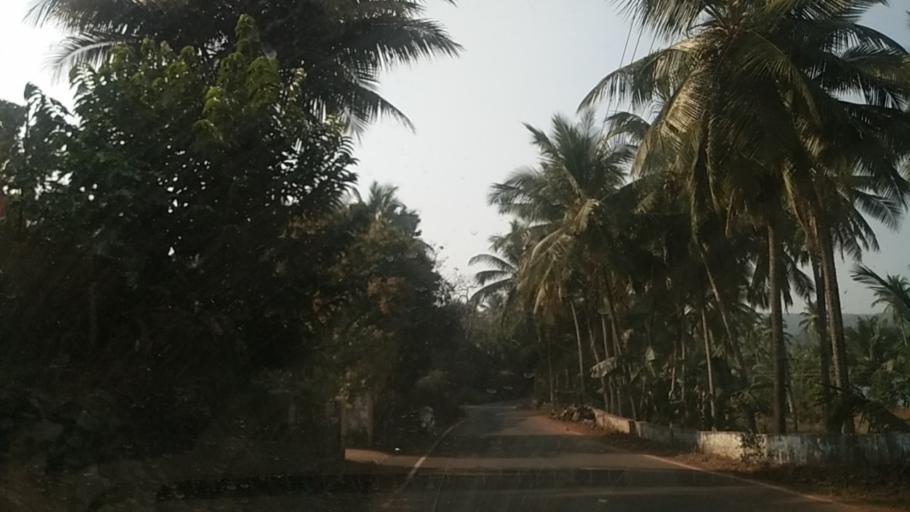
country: IN
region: Goa
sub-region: North Goa
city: Pernem
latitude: 15.7312
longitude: 73.7665
